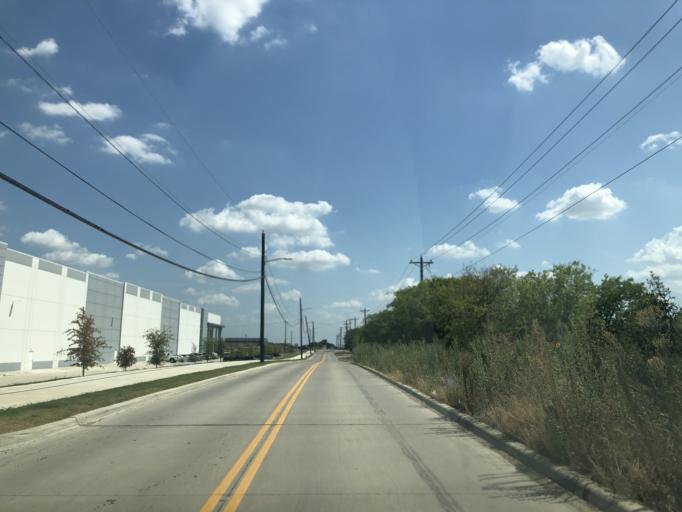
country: US
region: Texas
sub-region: Tarrant County
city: Haslet
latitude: 32.9362
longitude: -97.3228
